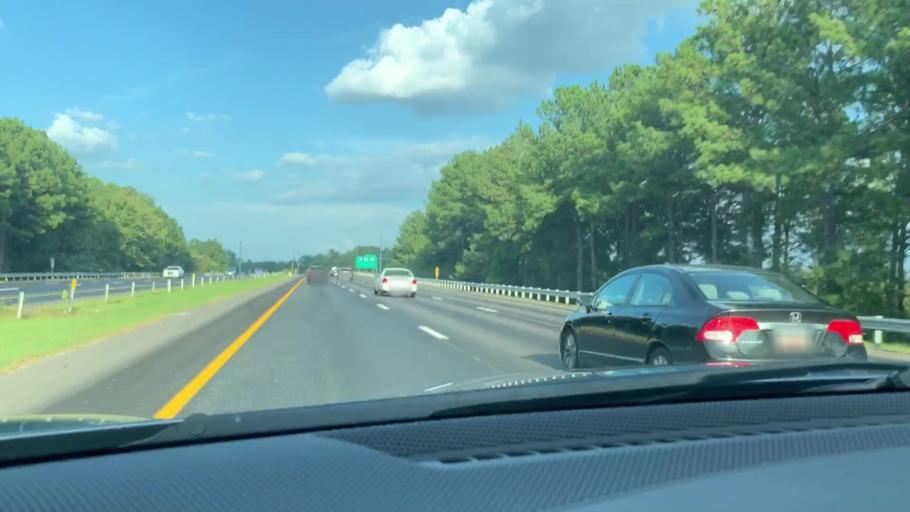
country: US
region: South Carolina
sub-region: Richland County
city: Forest Acres
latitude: 33.9540
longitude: -80.9610
